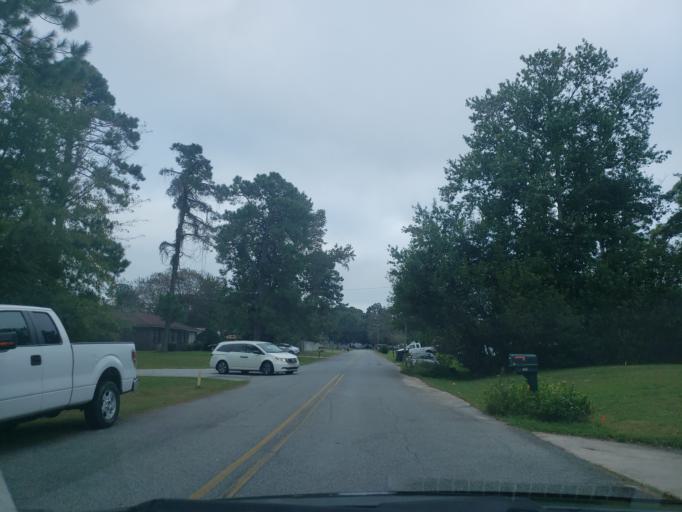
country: US
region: Georgia
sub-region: Chatham County
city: Montgomery
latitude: 31.9516
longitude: -81.1113
